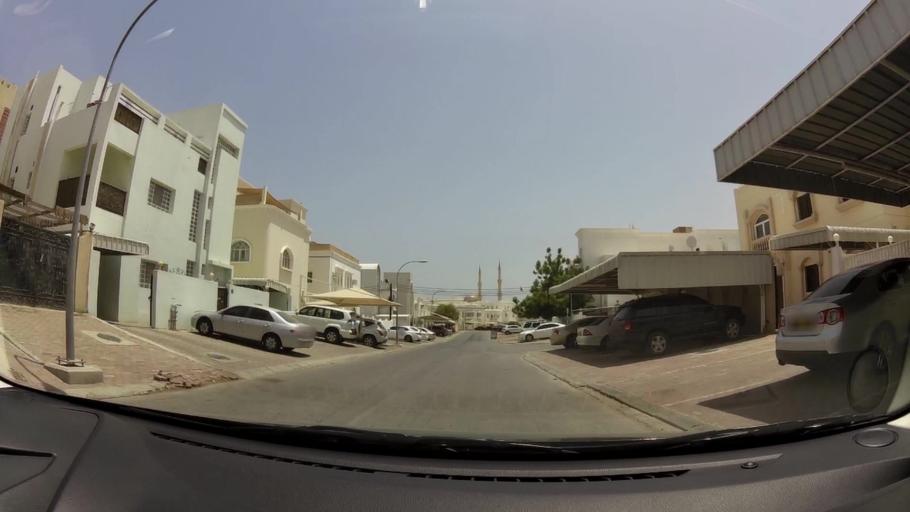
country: OM
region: Muhafazat Masqat
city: Bawshar
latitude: 23.5809
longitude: 58.4289
